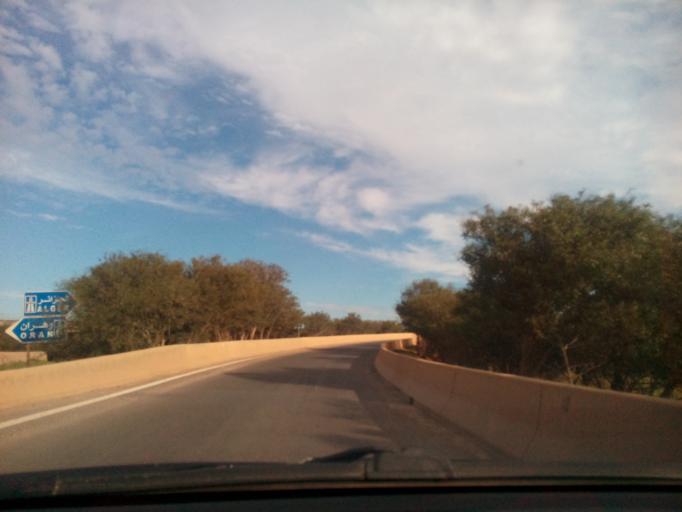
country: DZ
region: Mascara
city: Sig
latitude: 35.5422
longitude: -0.3782
